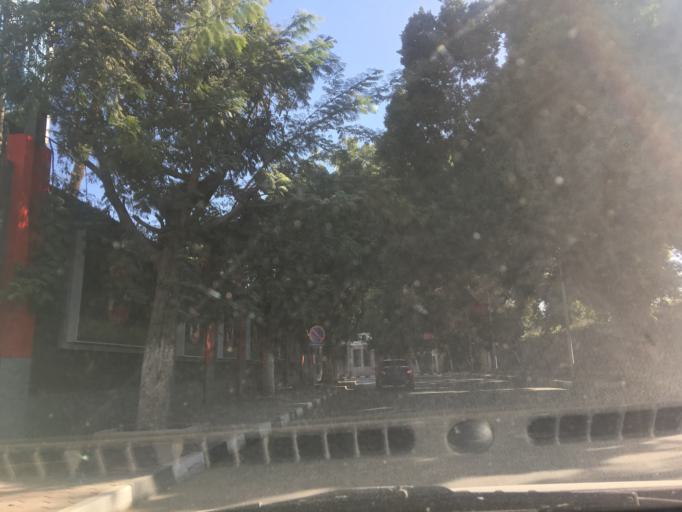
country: EG
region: Muhafazat al Qahirah
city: Cairo
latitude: 30.0437
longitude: 31.2233
